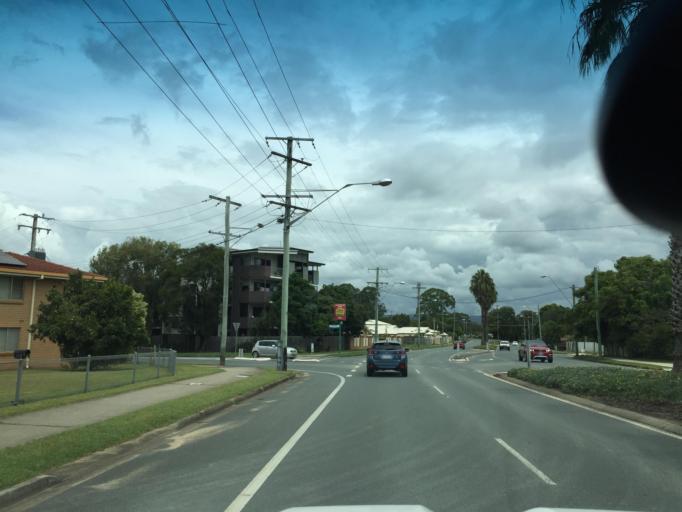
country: AU
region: Queensland
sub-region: Moreton Bay
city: Caboolture
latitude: -27.0849
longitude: 152.9444
